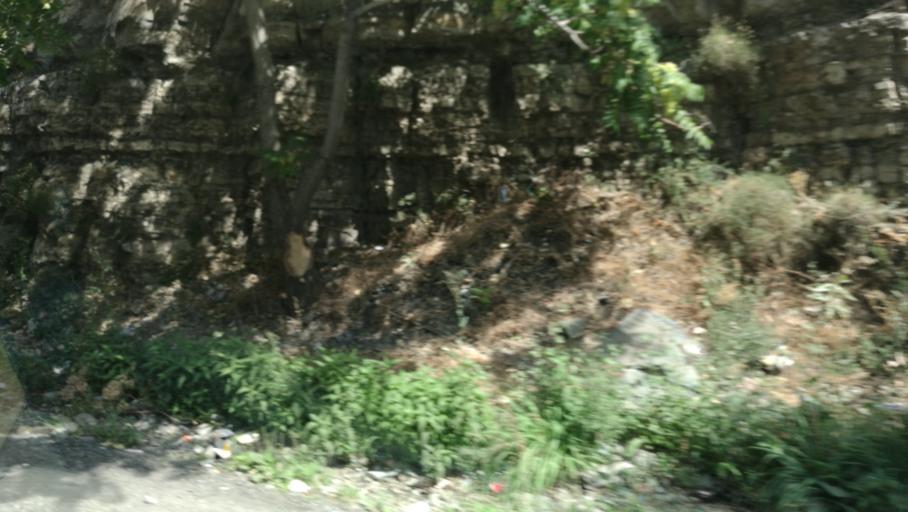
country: IR
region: Alborz
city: Karaj
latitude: 35.9387
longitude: 51.0700
